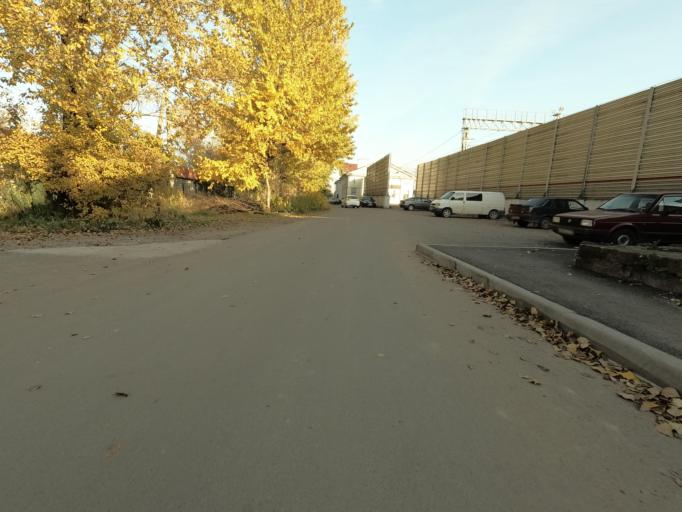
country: RU
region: Leningrad
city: Mga
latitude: 59.7561
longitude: 31.0605
